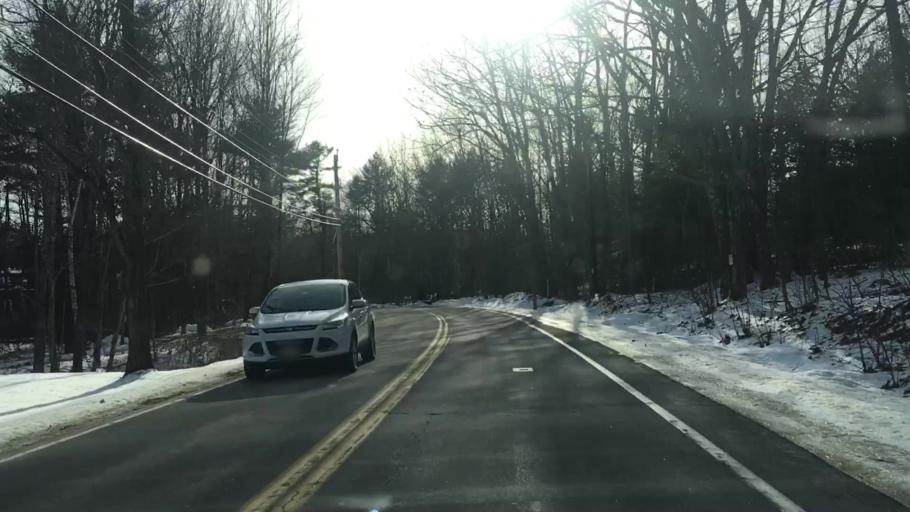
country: US
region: Maine
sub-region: Cumberland County
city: Westbrook
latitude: 43.7054
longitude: -70.3588
